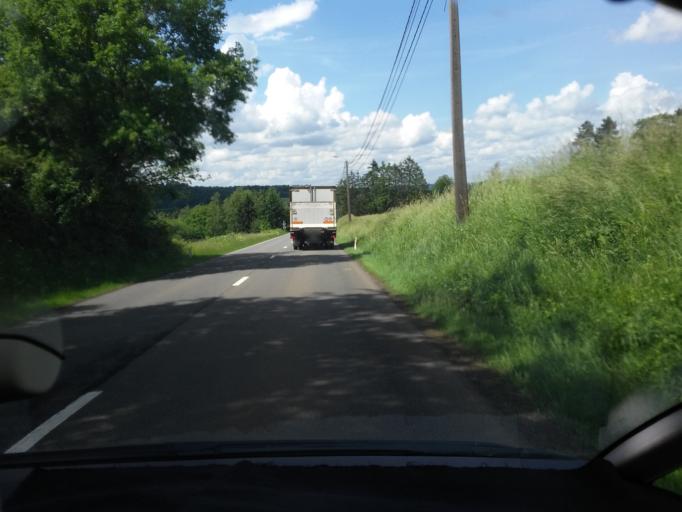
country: BE
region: Wallonia
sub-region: Province de Namur
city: Rochefort
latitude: 50.1385
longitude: 5.2249
